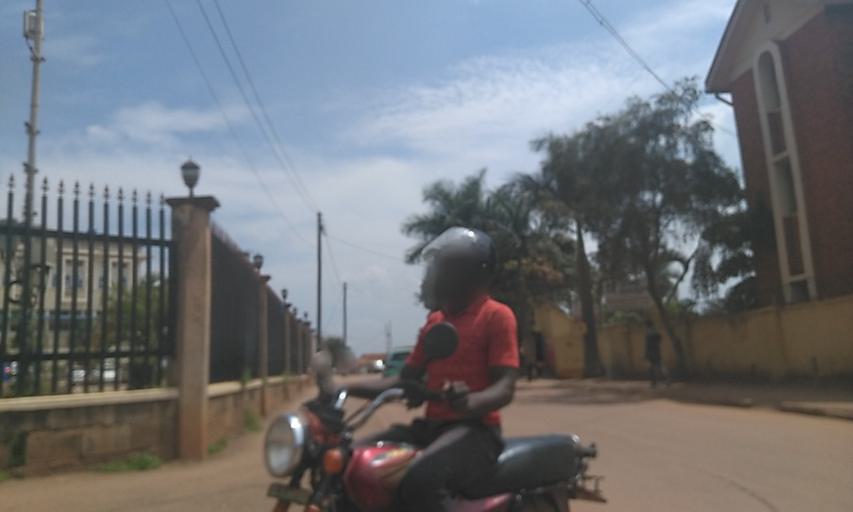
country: UG
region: Central Region
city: Kampala Central Division
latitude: 0.3088
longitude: 32.5575
